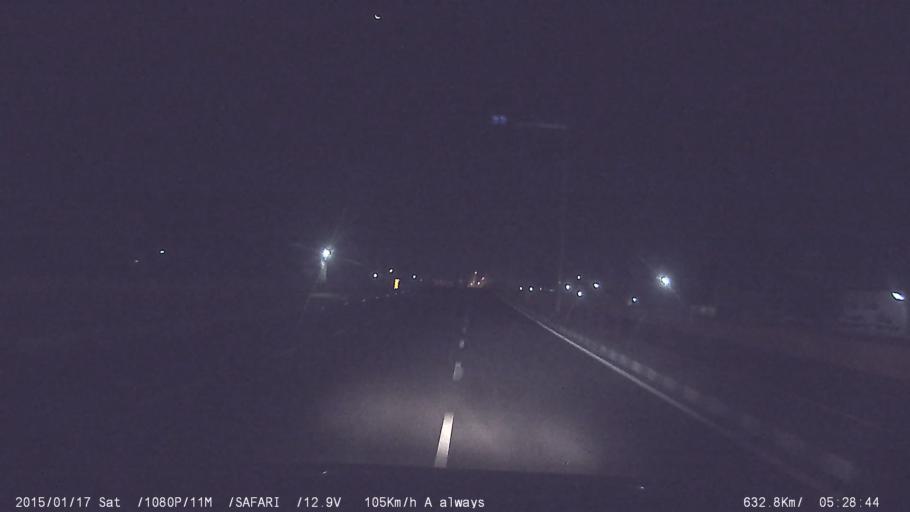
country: IN
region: Tamil Nadu
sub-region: Vellore
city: Arcot
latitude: 12.9229
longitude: 79.2761
